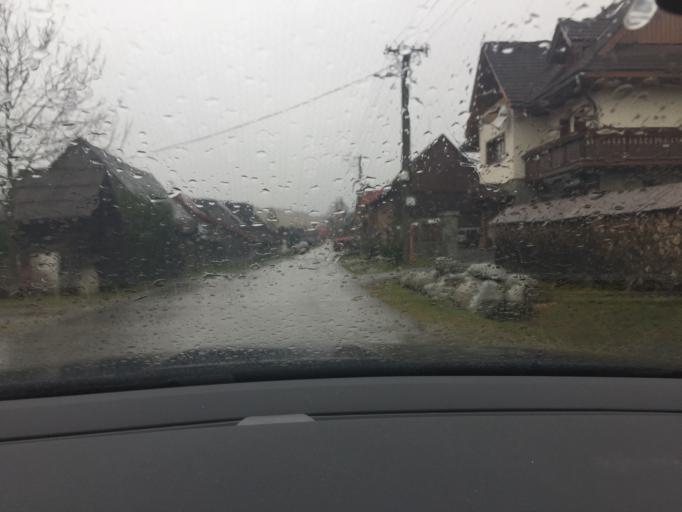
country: SK
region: Presovsky
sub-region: Okres Poprad
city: Zdiar
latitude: 49.2706
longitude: 20.2683
